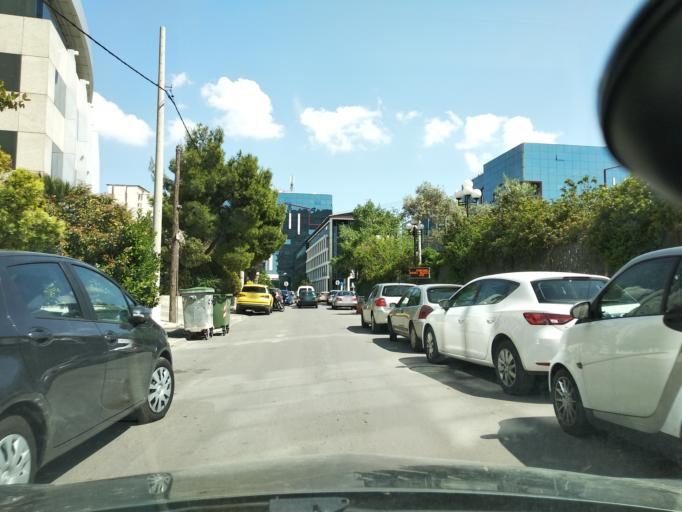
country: GR
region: Attica
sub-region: Nomarchia Athinas
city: Marousi
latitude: 38.0455
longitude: 23.8053
